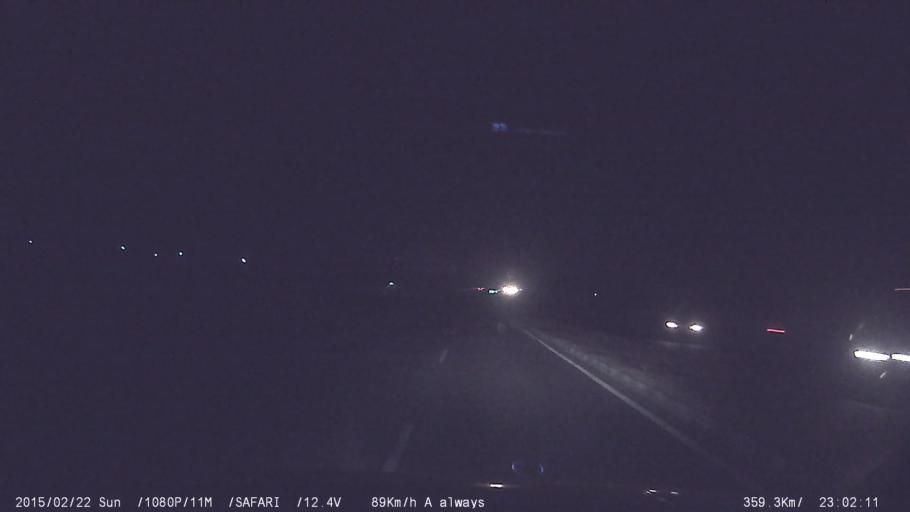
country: IN
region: Tamil Nadu
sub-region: Namakkal
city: Rasipuram
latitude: 11.3731
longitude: 78.1631
